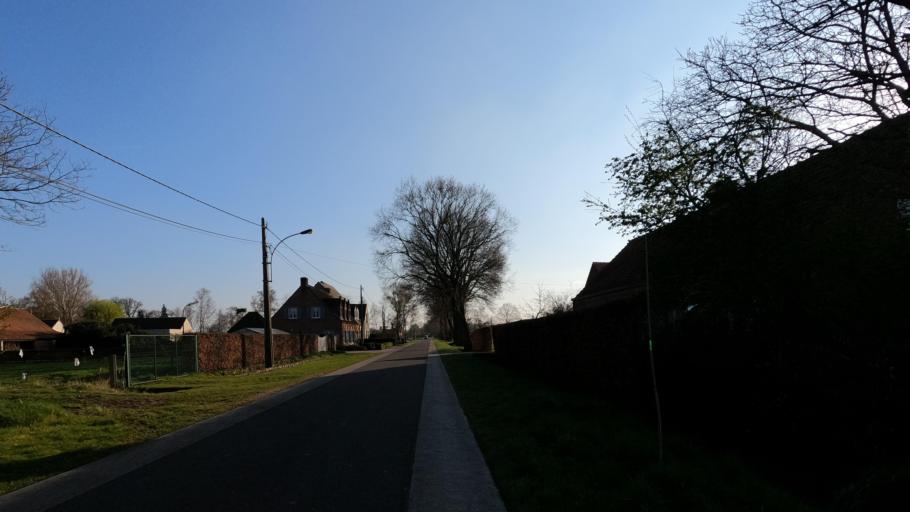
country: BE
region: Flanders
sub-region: Provincie Antwerpen
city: Beerse
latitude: 51.3328
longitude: 4.8326
